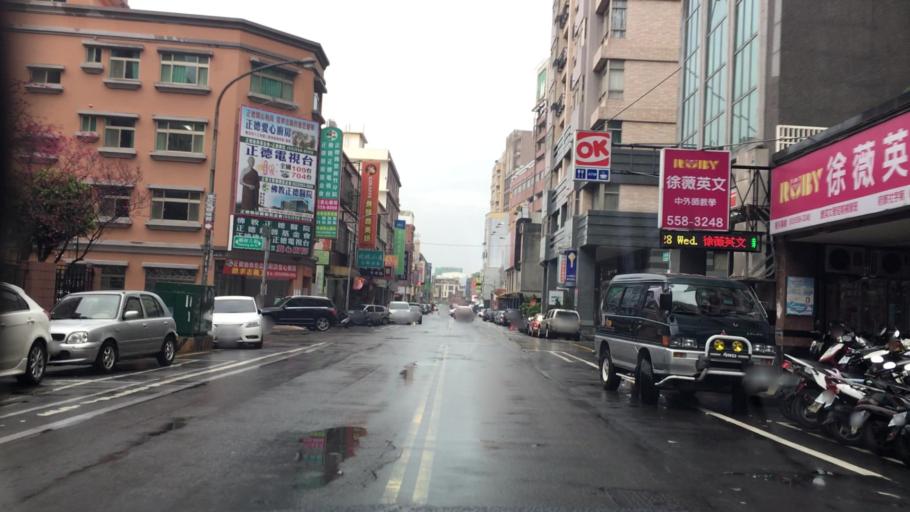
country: TW
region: Taiwan
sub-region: Hsinchu
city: Zhubei
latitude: 24.8249
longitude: 121.0101
